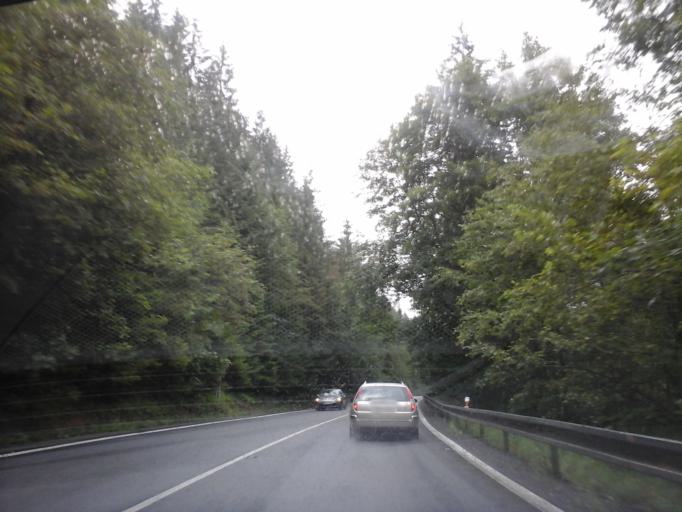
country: SK
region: Presovsky
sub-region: Okres Poprad
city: Poprad
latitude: 48.9358
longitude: 20.2851
